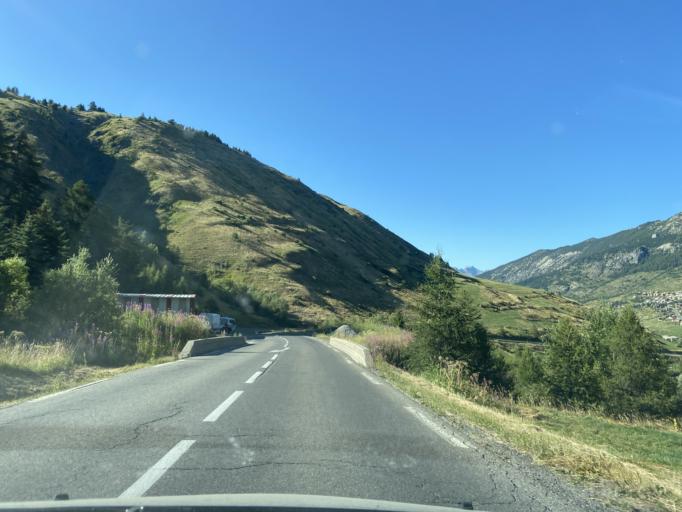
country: FR
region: Provence-Alpes-Cote d'Azur
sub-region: Departement des Hautes-Alpes
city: Guillestre
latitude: 44.5817
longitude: 6.6838
